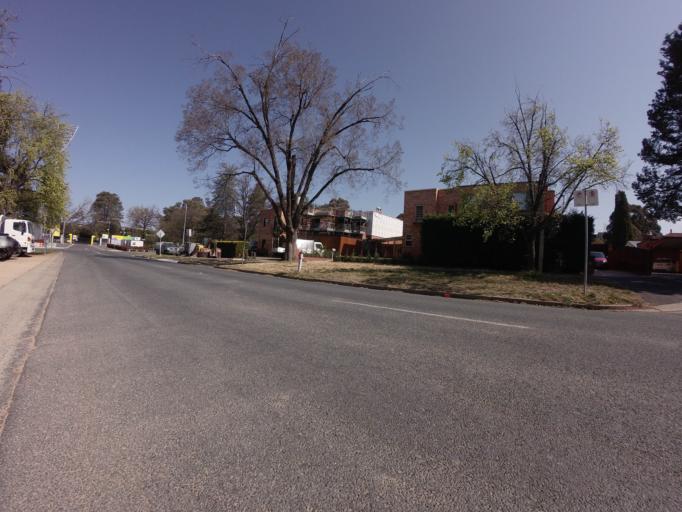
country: AU
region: Australian Capital Territory
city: Forrest
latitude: -35.3164
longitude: 149.1331
